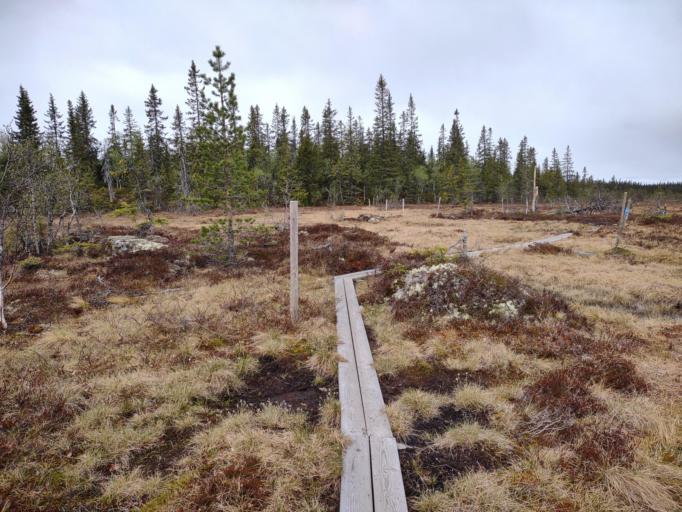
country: NO
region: Oppland
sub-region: Gran
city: Jaren
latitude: 60.4287
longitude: 10.6696
